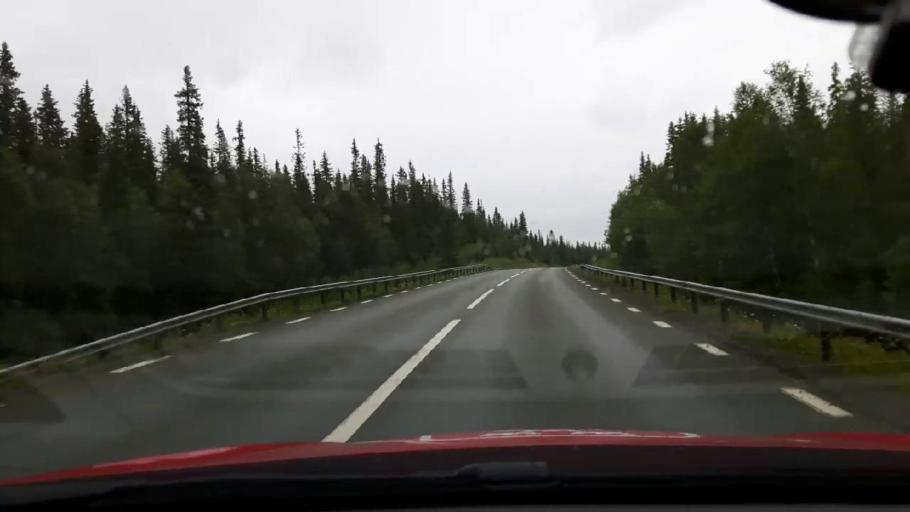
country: NO
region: Nord-Trondelag
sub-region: Meraker
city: Meraker
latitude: 63.2738
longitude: 12.2744
